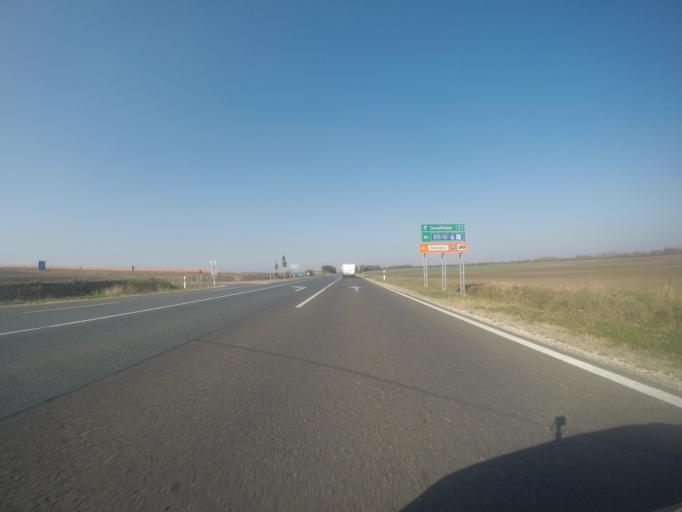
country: HU
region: Tolna
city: Madocsa
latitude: 46.7259
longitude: 18.8840
